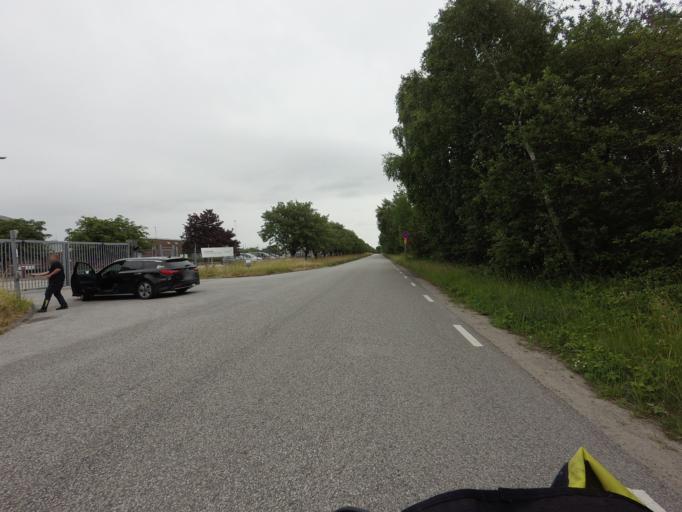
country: SE
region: Skane
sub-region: Malmo
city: Bunkeflostrand
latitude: 55.5237
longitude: 12.9032
